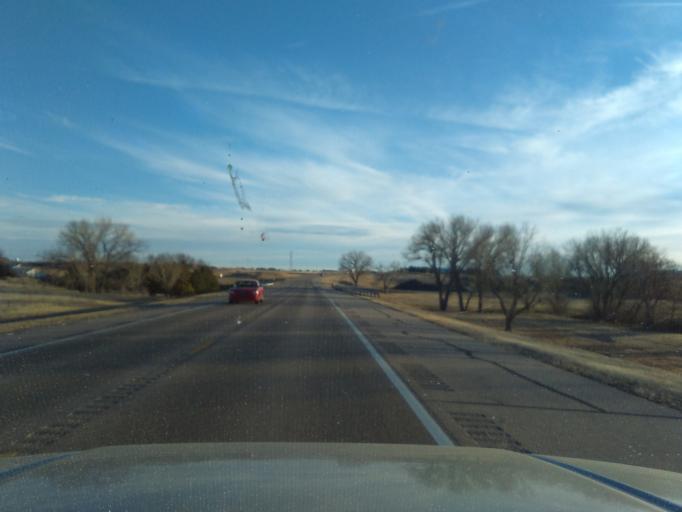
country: US
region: Kansas
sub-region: Logan County
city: Oakley
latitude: 39.1504
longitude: -100.8695
